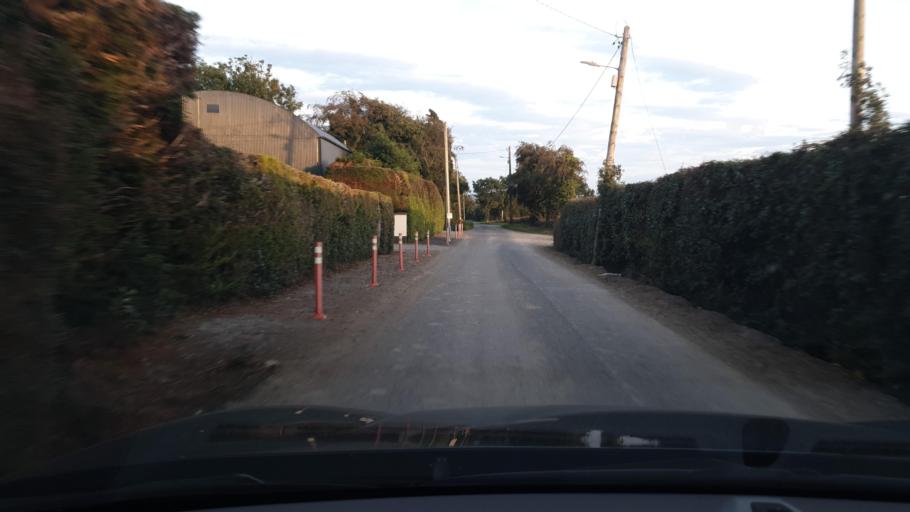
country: IE
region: Leinster
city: Balrothery
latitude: 53.5686
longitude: -6.2408
